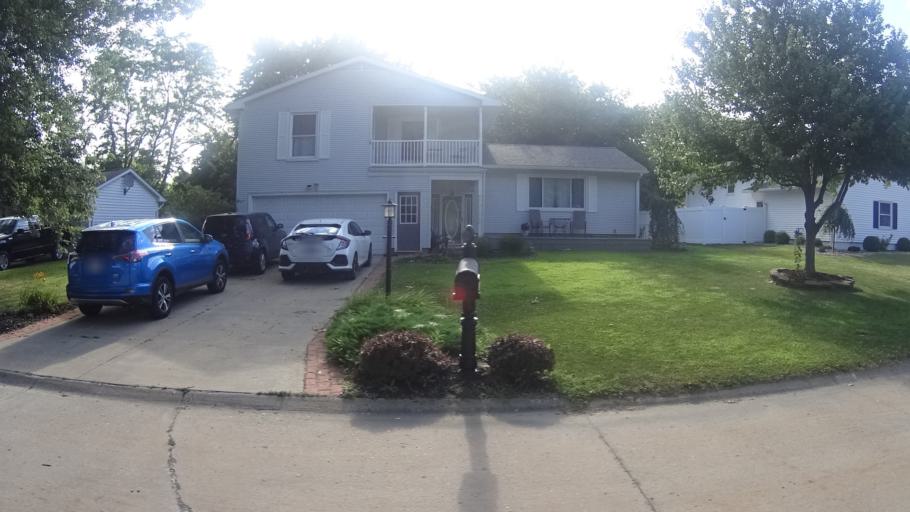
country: US
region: Ohio
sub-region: Erie County
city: Sandusky
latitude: 41.4289
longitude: -82.6798
